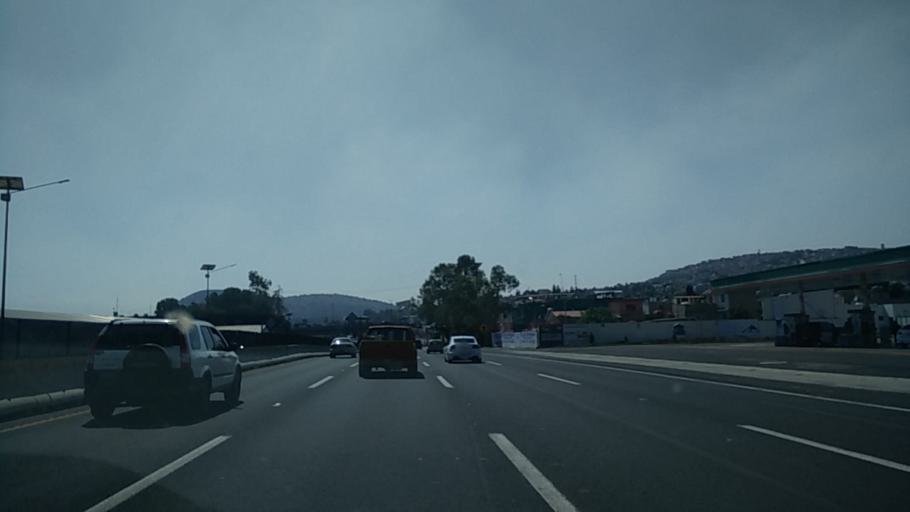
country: MX
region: Mexico
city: Ecatepec
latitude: 19.5718
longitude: -99.0516
